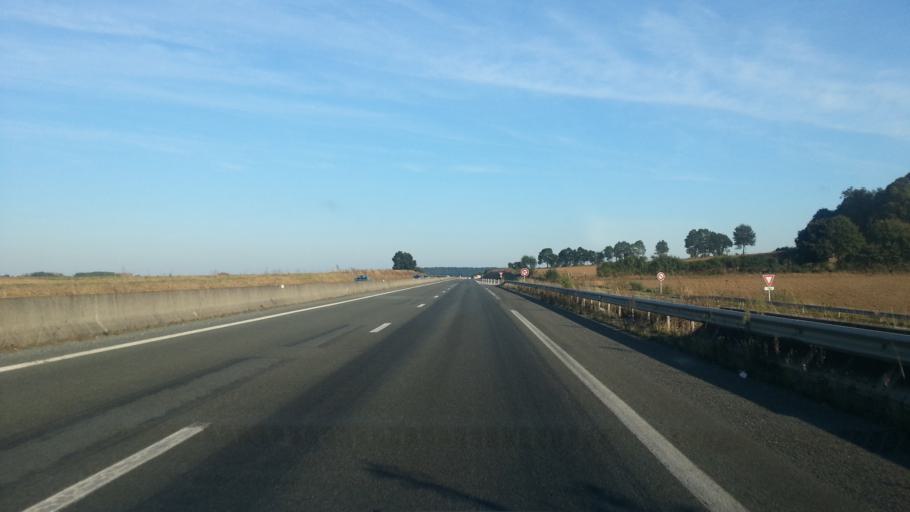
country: FR
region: Picardie
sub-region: Departement de l'Oise
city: Warluis
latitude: 49.4184
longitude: 2.1667
